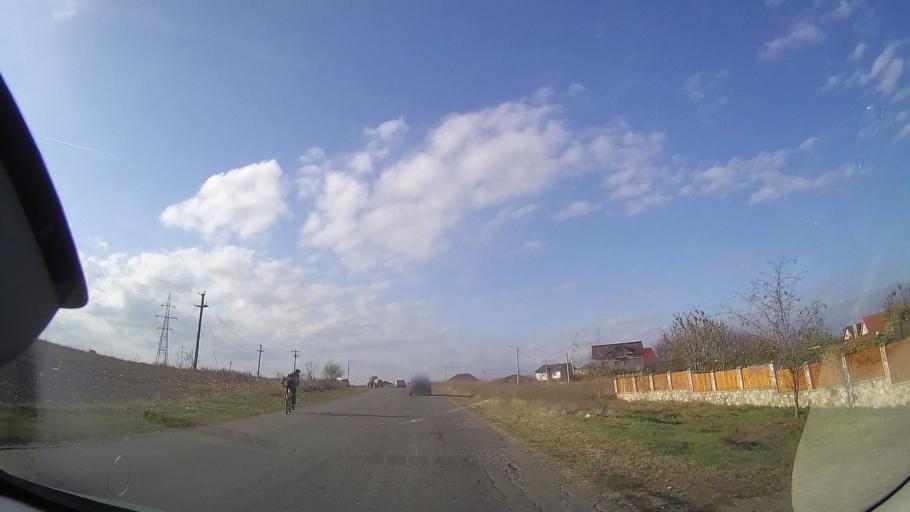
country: RO
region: Constanta
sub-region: Comuna Limanu
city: Limanu
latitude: 43.7929
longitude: 28.5449
